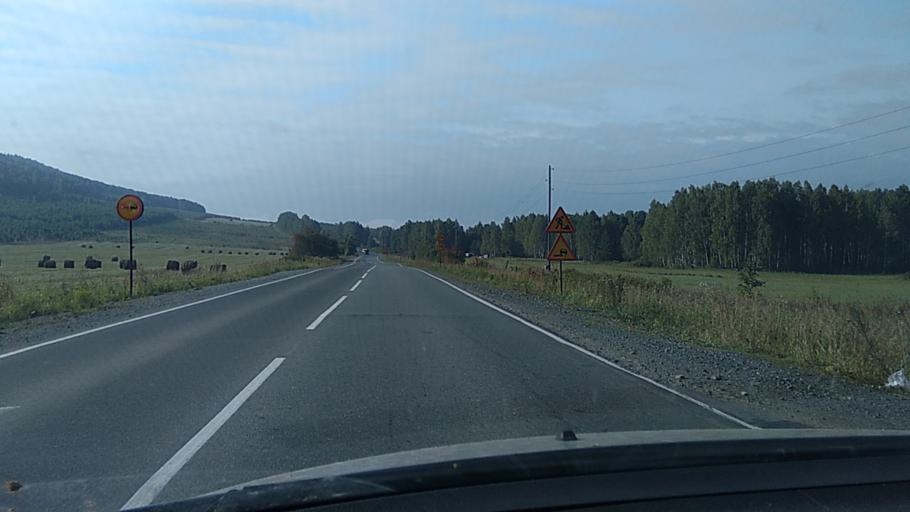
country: RU
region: Chelyabinsk
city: Karabash
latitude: 55.3815
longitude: 60.2552
